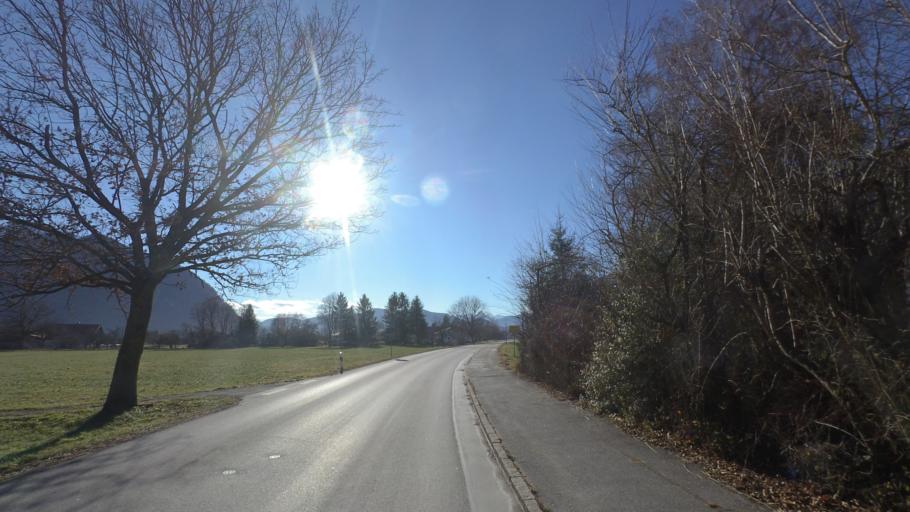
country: DE
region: Bavaria
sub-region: Upper Bavaria
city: Staudach-Egerndach
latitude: 47.7926
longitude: 12.4712
